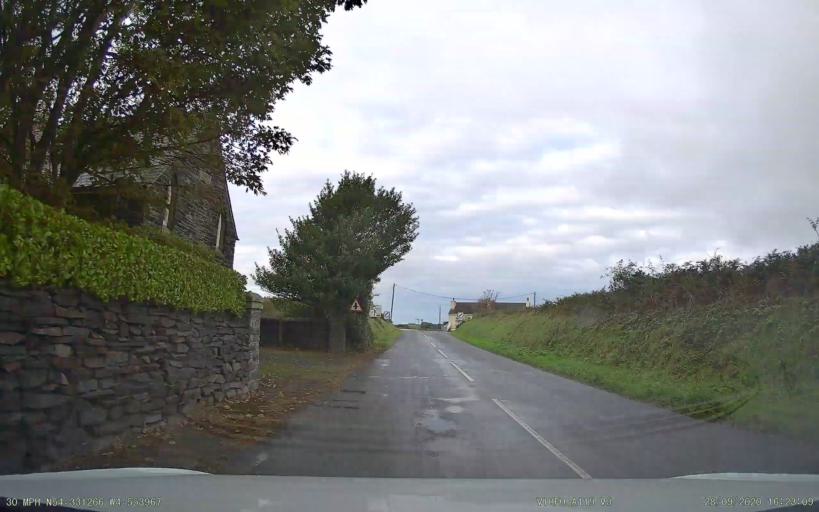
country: IM
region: Ramsey
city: Ramsey
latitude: 54.3313
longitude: -4.5540
